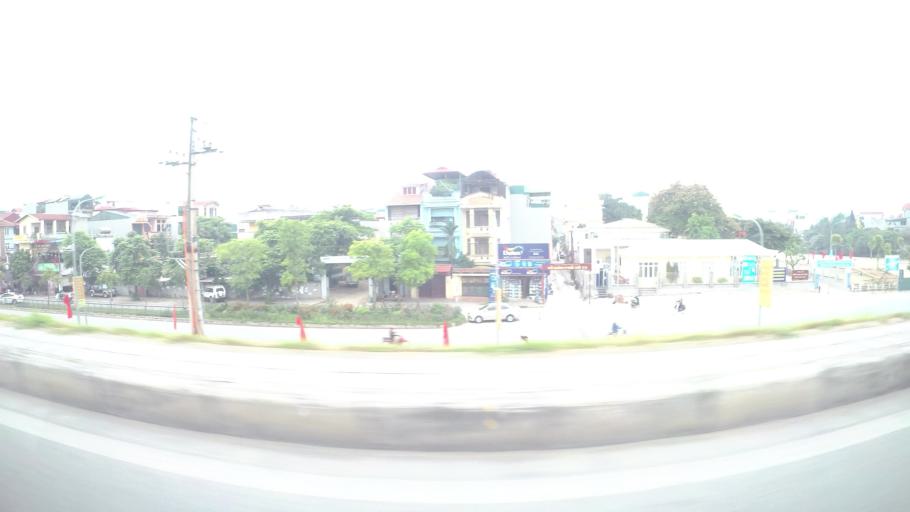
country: VN
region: Ha Noi
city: Hoan Kiem
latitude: 21.0574
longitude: 105.8654
